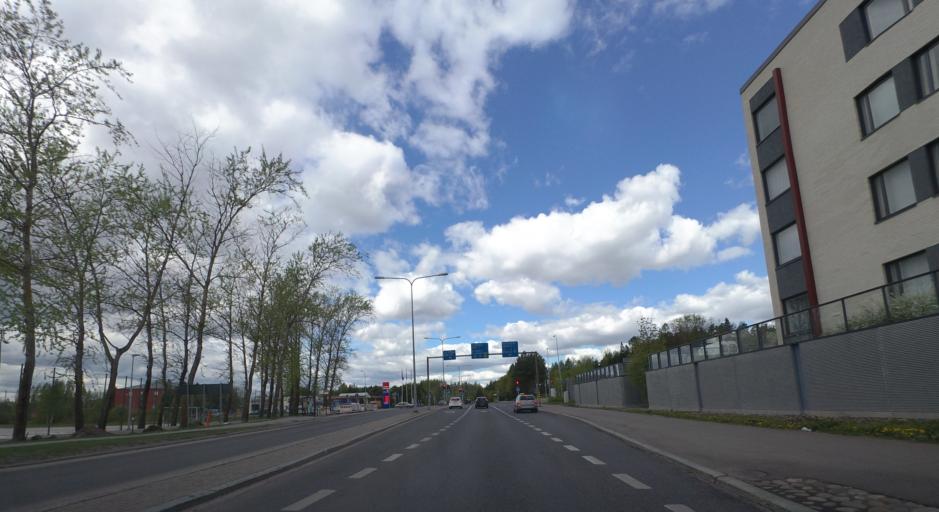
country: FI
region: Uusimaa
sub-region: Helsinki
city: Vantaa
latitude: 60.3017
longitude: 25.0241
